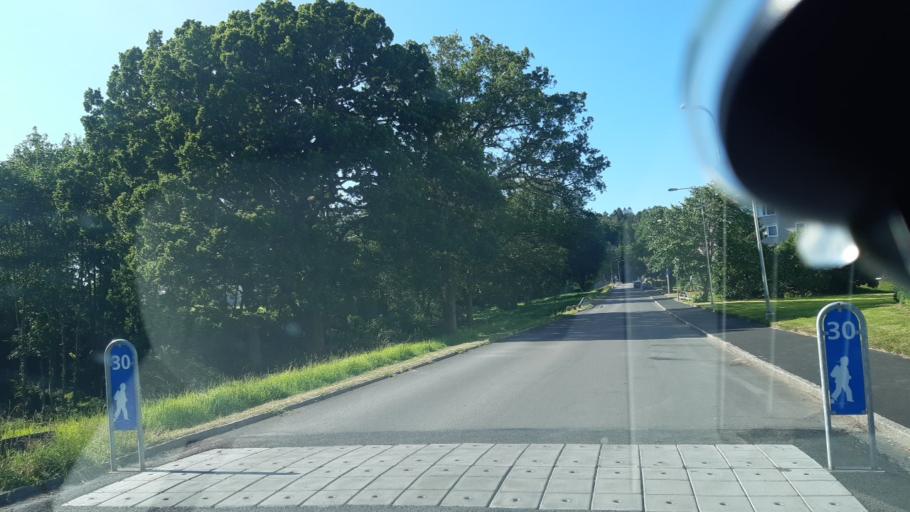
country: SE
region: Vaestra Goetaland
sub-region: Goteborg
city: Eriksbo
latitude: 57.7695
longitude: 12.0345
